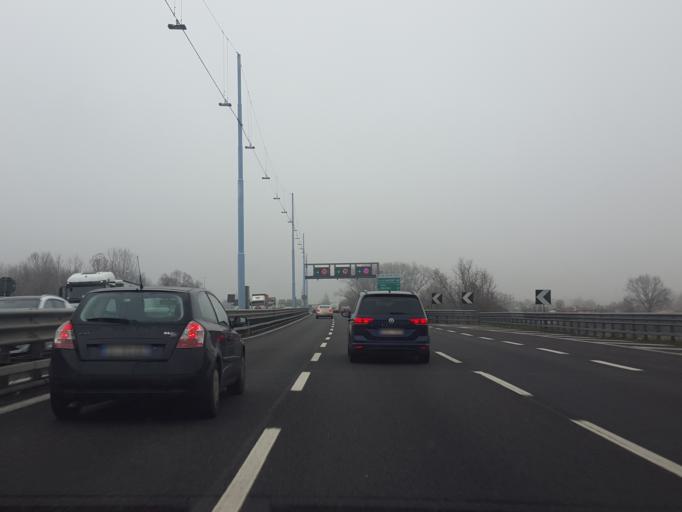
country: IT
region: Veneto
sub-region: Provincia di Treviso
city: Mogliano Veneto
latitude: 45.5177
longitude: 12.2489
